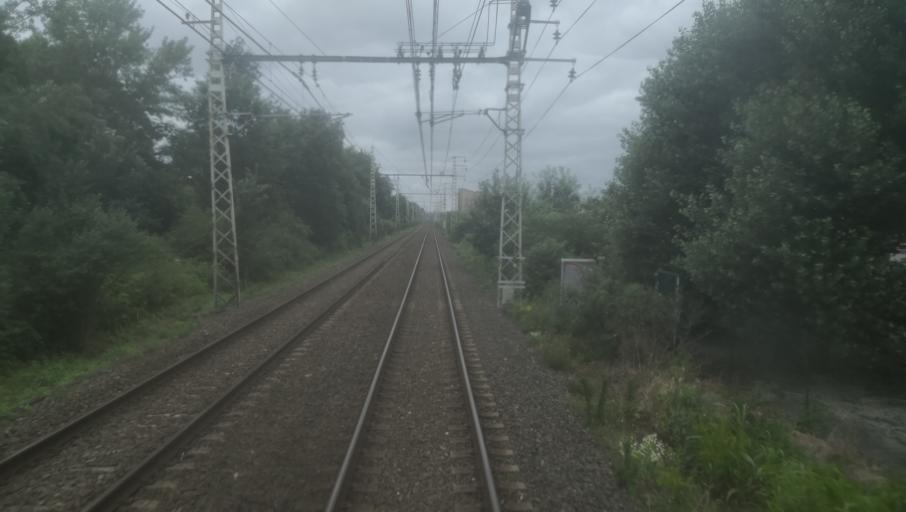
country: FR
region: Midi-Pyrenees
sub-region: Departement de la Haute-Garonne
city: Lespinasse
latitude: 43.7122
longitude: 1.3857
